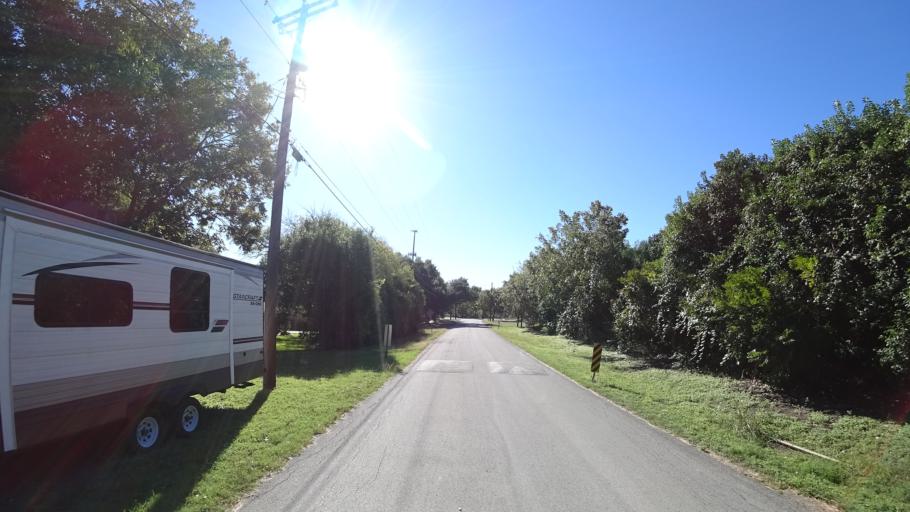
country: US
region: Texas
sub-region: Travis County
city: Manor
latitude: 30.3313
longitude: -97.6550
